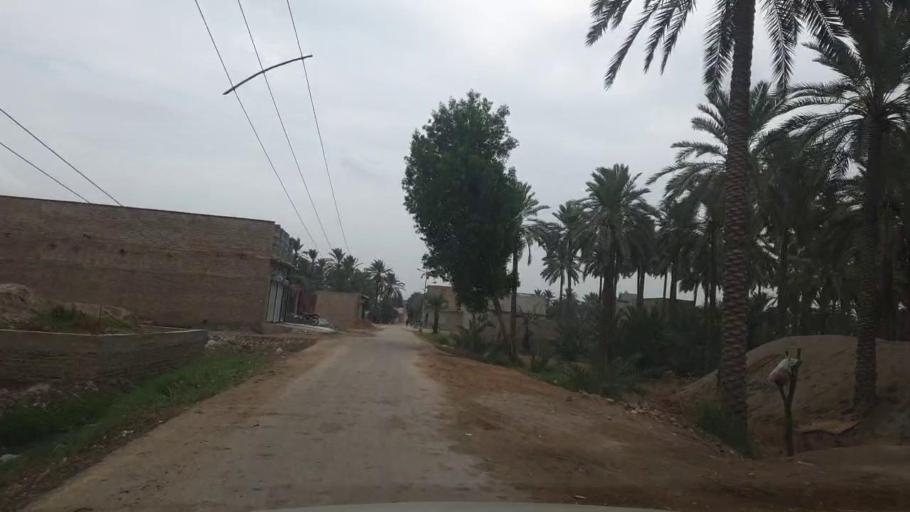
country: PK
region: Sindh
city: Khairpur
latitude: 27.5491
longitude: 68.7509
